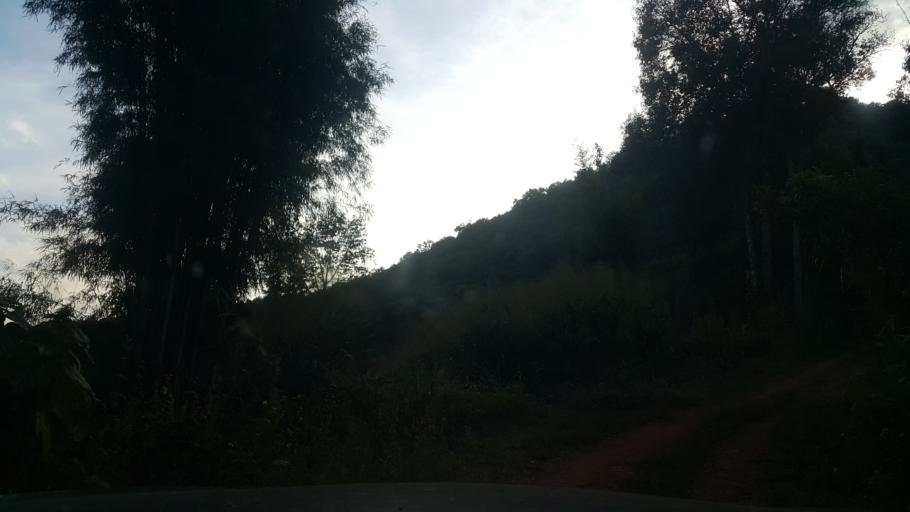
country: TH
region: Chiang Mai
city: Samoeng
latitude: 19.0175
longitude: 98.6507
